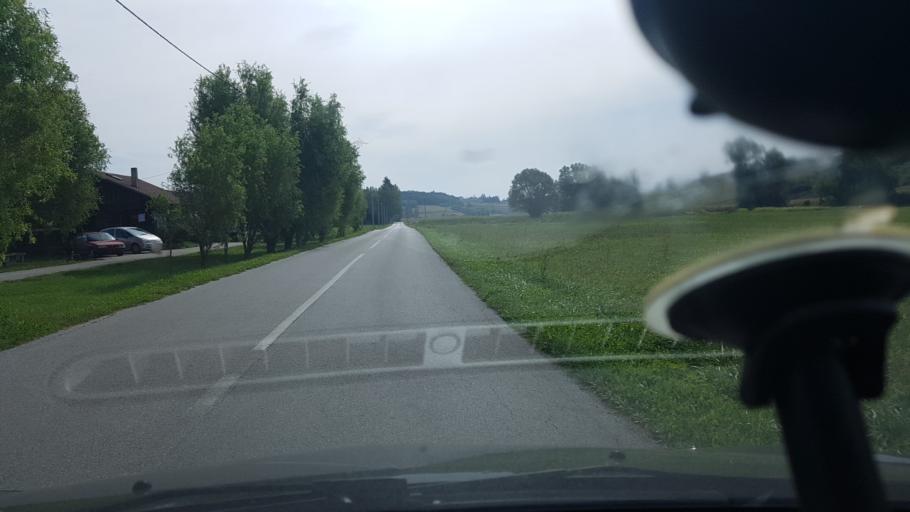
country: HR
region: Varazdinska
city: Remetinec
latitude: 46.1079
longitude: 16.2547
